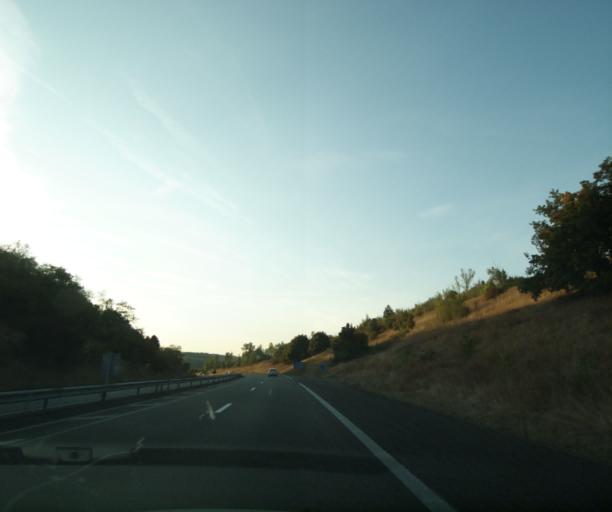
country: FR
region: Aquitaine
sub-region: Departement du Lot-et-Garonne
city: Boe
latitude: 44.1442
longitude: 0.6324
